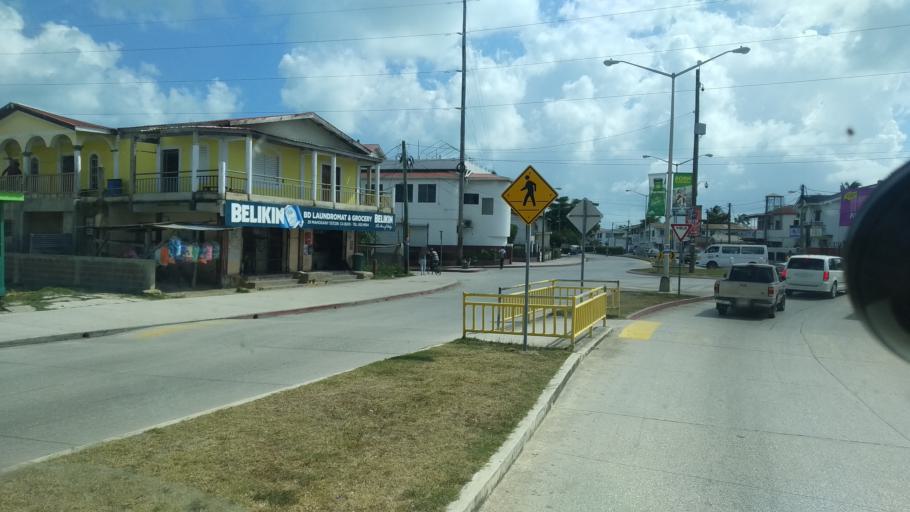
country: BZ
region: Belize
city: Belize City
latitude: 17.5007
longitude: -88.1987
